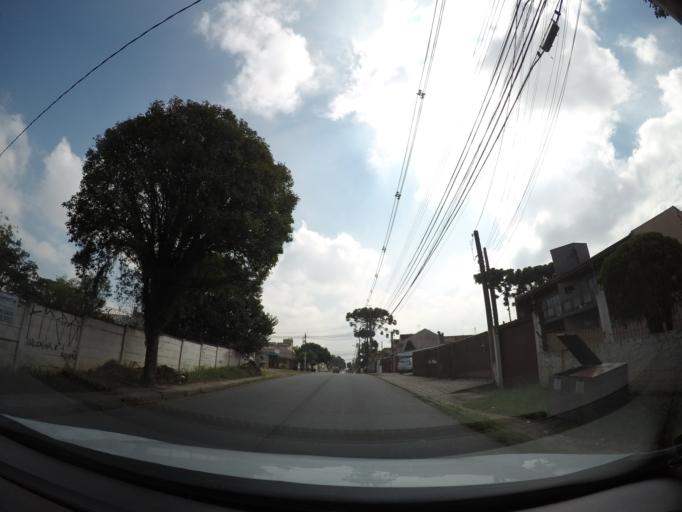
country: BR
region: Parana
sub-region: Sao Jose Dos Pinhais
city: Sao Jose dos Pinhais
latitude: -25.5032
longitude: -49.2492
